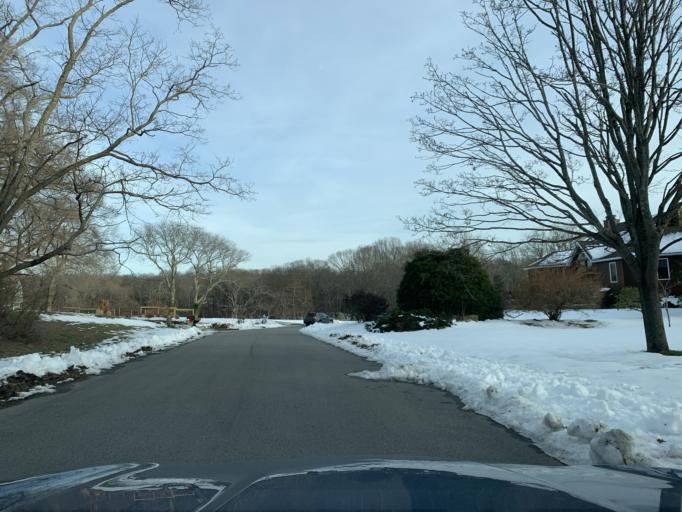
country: US
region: Rhode Island
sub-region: Washington County
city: North Kingstown
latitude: 41.5887
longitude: -71.4406
